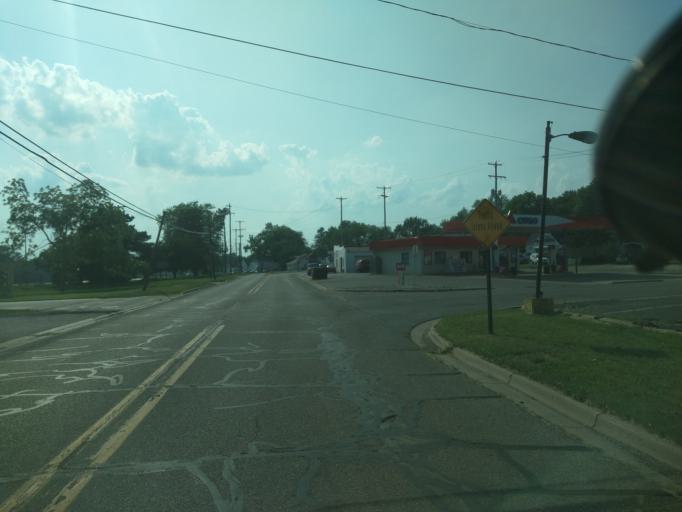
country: US
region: Michigan
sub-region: Jackson County
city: Jackson
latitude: 42.2541
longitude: -84.4368
